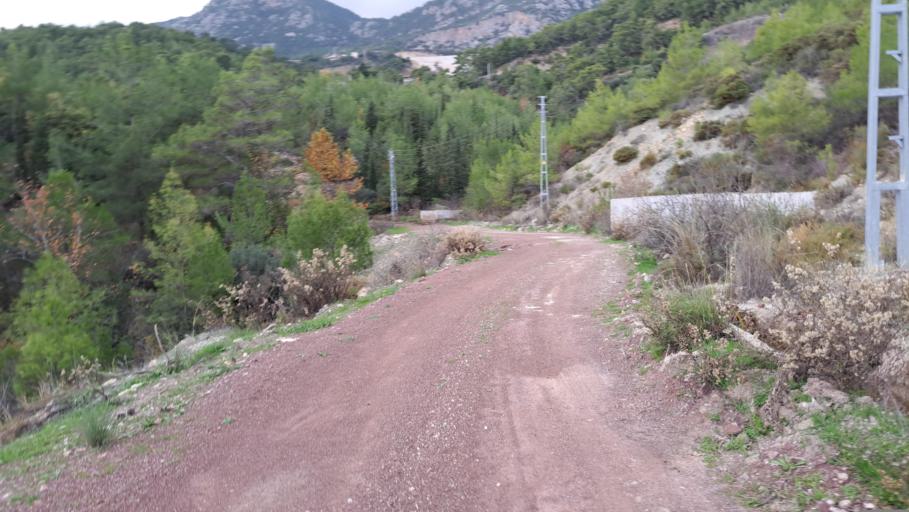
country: TR
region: Antalya
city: Tekirova
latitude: 36.3999
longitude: 30.4297
